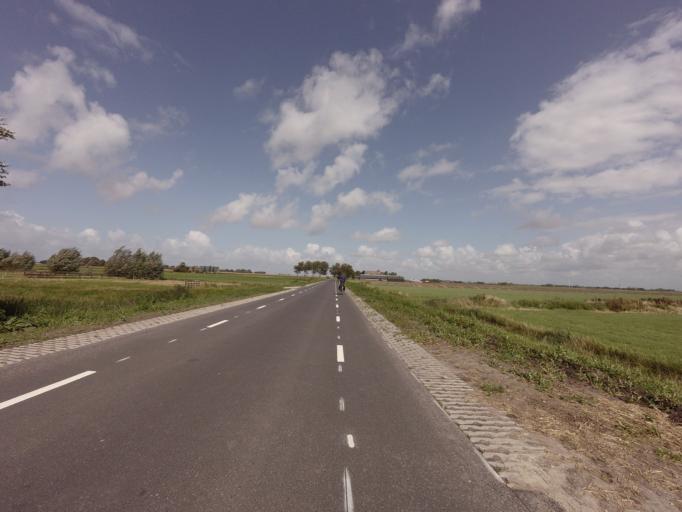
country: NL
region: Friesland
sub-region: Gemeente Harlingen
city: Harlingen
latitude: 53.1514
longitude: 5.4772
